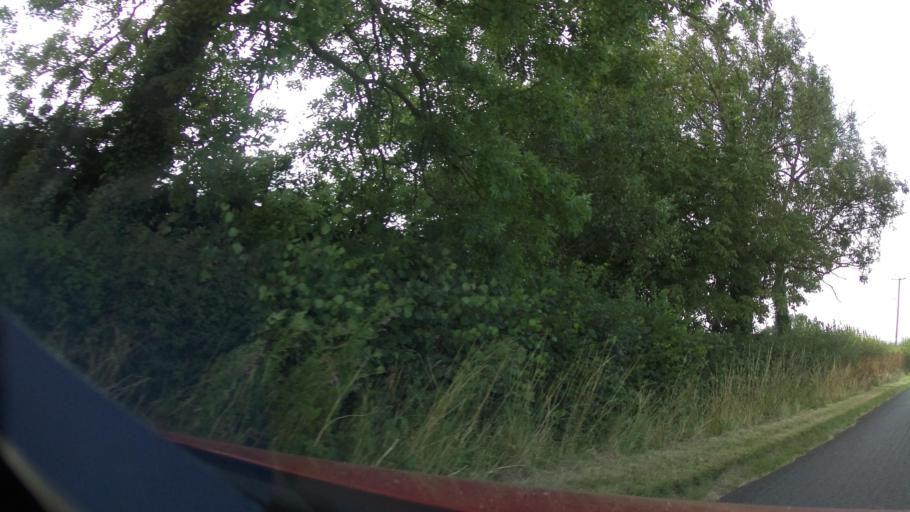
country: GB
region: England
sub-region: Bath and North East Somerset
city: Compton Martin
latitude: 51.3251
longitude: -2.6406
